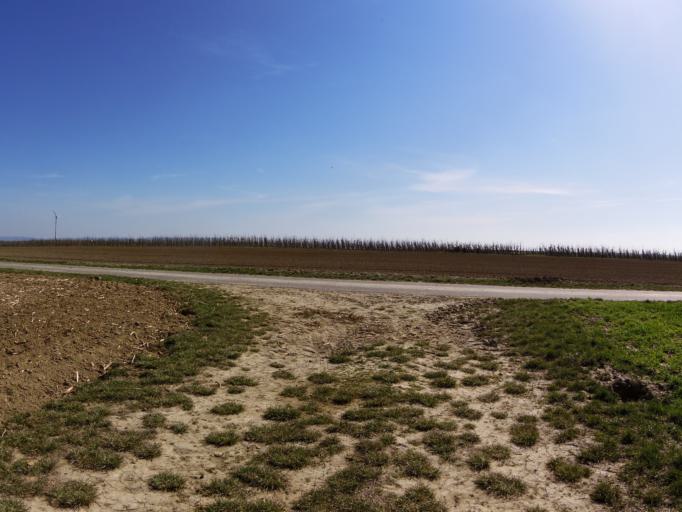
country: DE
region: Bavaria
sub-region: Regierungsbezirk Unterfranken
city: Prosselsheim
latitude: 49.8458
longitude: 10.1295
